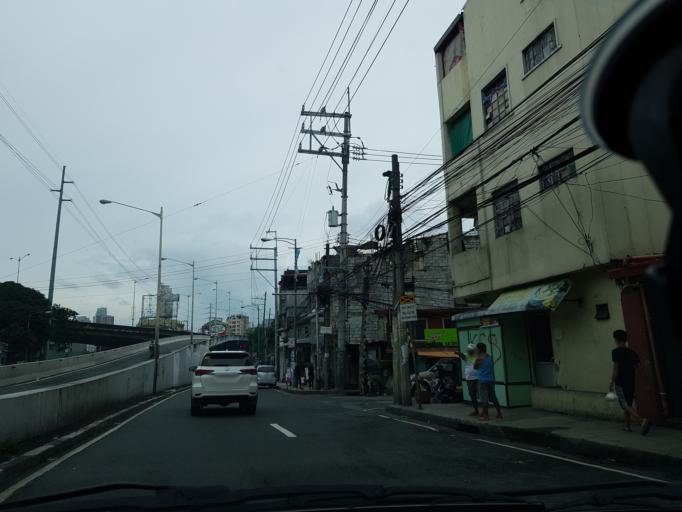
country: PH
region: Metro Manila
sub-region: Makati City
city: Makati City
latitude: 14.5575
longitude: 121.0432
